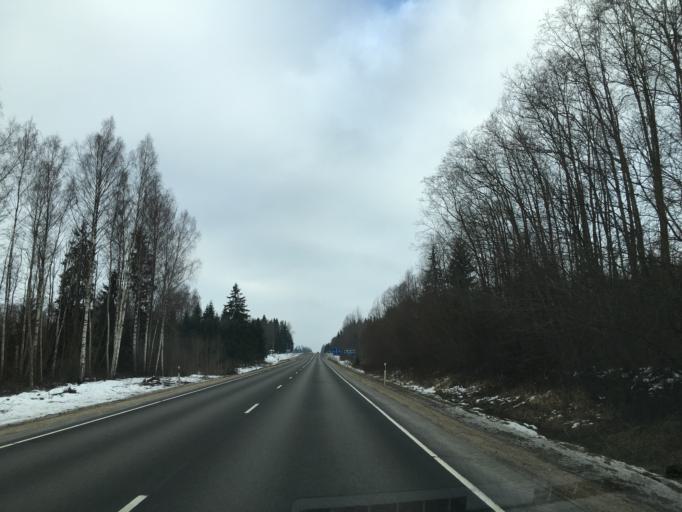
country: EE
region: Tartu
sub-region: Elva linn
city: Elva
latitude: 58.2235
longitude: 26.3699
